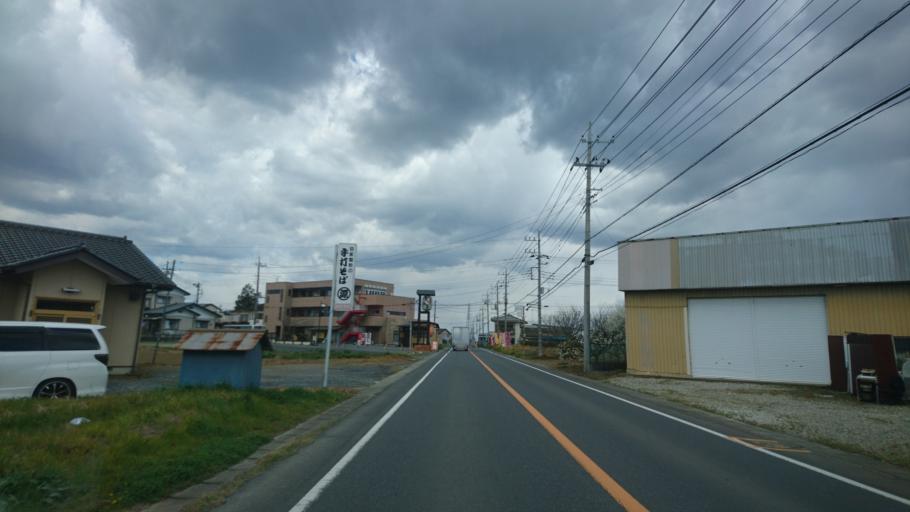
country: JP
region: Ibaraki
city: Yuki
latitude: 36.2386
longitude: 139.9320
